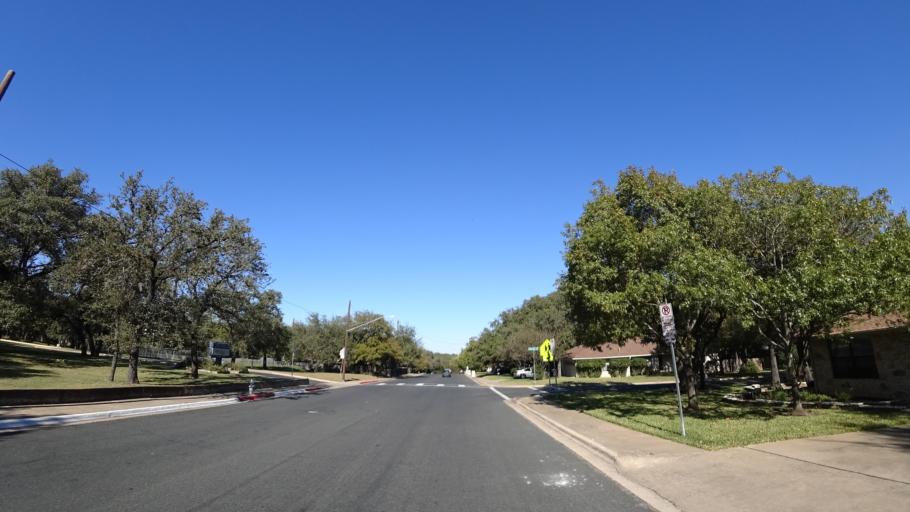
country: US
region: Texas
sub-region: Williamson County
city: Jollyville
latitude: 30.4191
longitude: -97.7679
